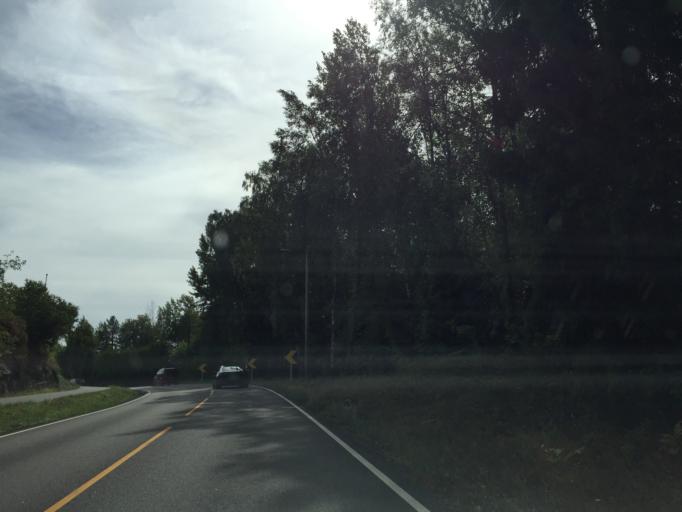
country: NO
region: Ostfold
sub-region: Fredrikstad
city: Fredrikstad
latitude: 59.1572
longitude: 10.9316
